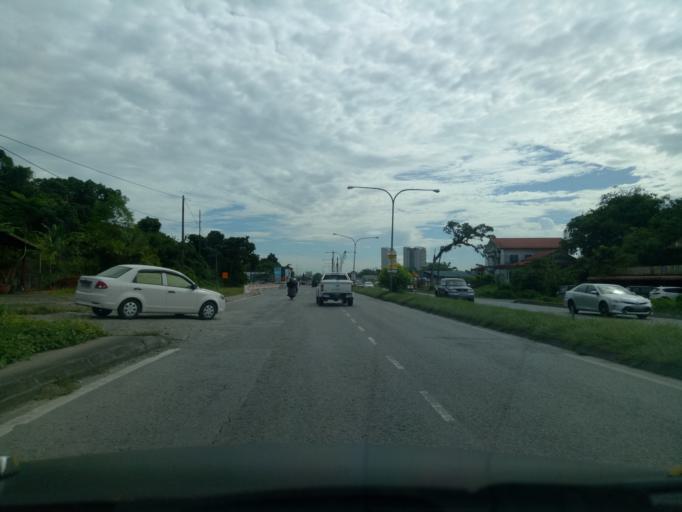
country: MY
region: Sarawak
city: Kuching
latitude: 1.4970
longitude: 110.3317
